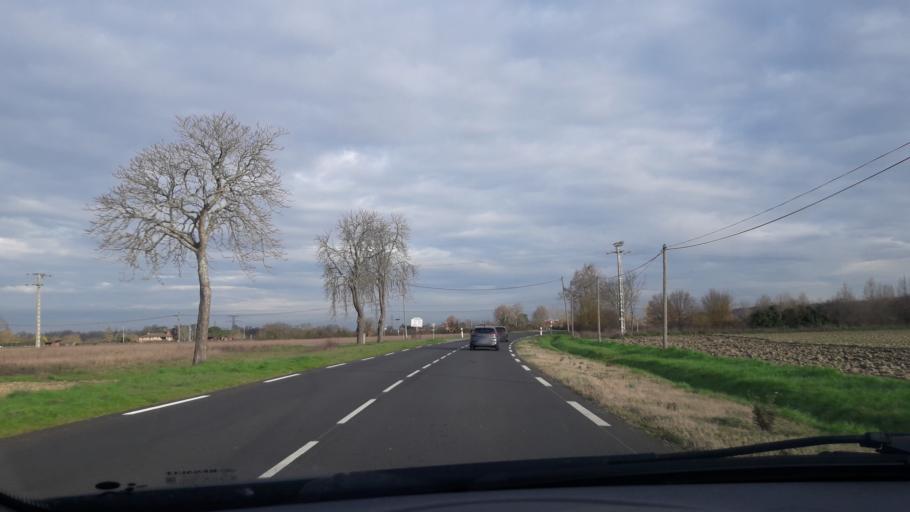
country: FR
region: Midi-Pyrenees
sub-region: Departement de la Haute-Garonne
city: Ondes
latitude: 43.7936
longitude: 1.2965
